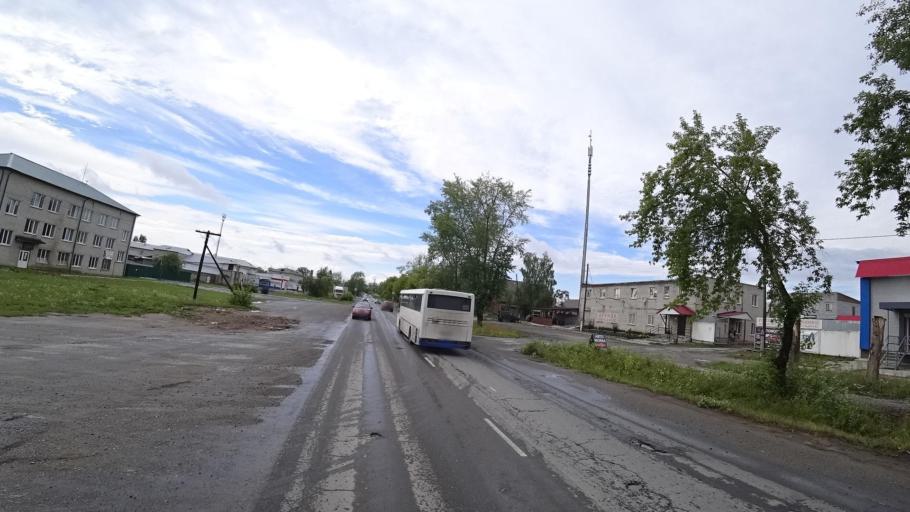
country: RU
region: Sverdlovsk
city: Kamyshlov
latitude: 56.8450
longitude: 62.7654
